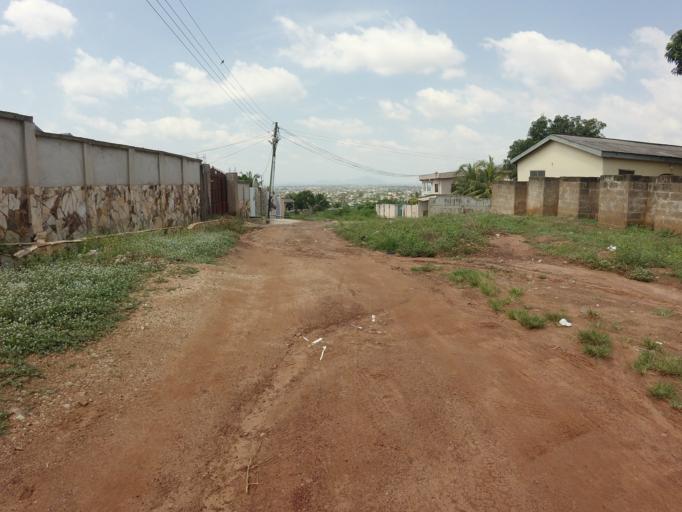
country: GH
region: Greater Accra
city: Gbawe
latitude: 5.6194
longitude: -0.3113
